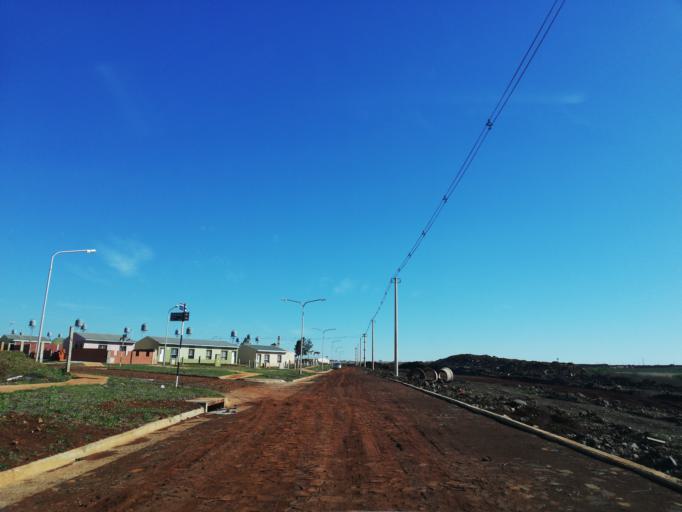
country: AR
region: Misiones
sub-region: Departamento de Capital
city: Posadas
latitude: -27.3985
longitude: -55.9913
